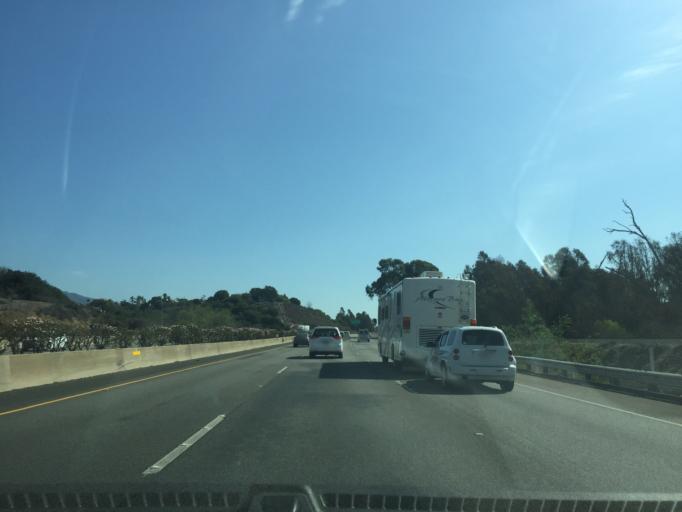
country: US
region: California
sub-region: Santa Barbara County
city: Goleta
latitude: 34.4421
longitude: -119.7781
